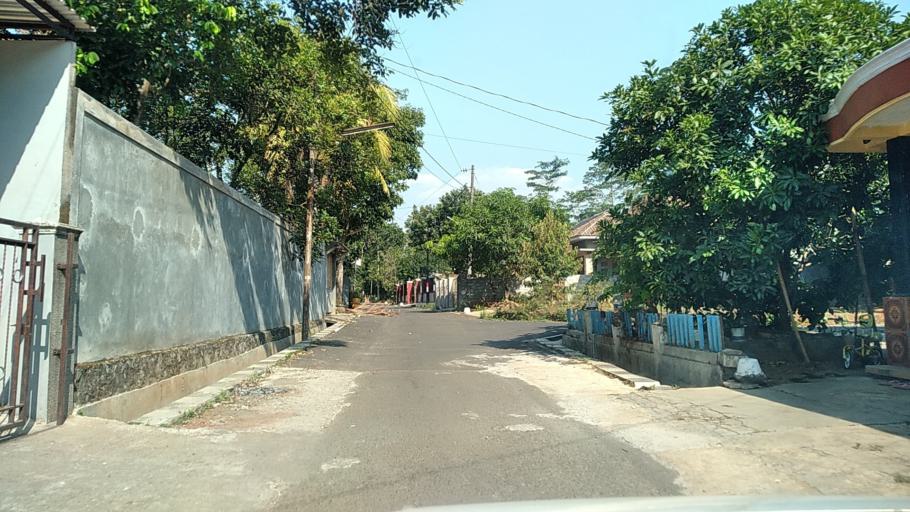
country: ID
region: Central Java
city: Ungaran
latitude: -7.0762
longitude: 110.3695
